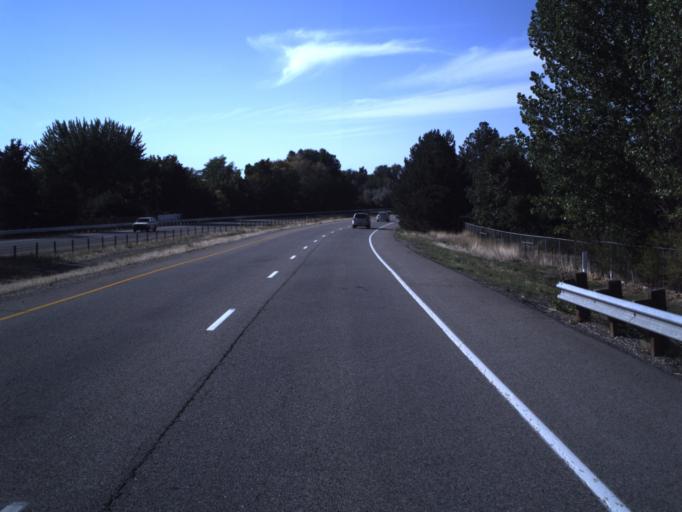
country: US
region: Utah
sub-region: Salt Lake County
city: Holladay
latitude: 40.6451
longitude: -111.8441
